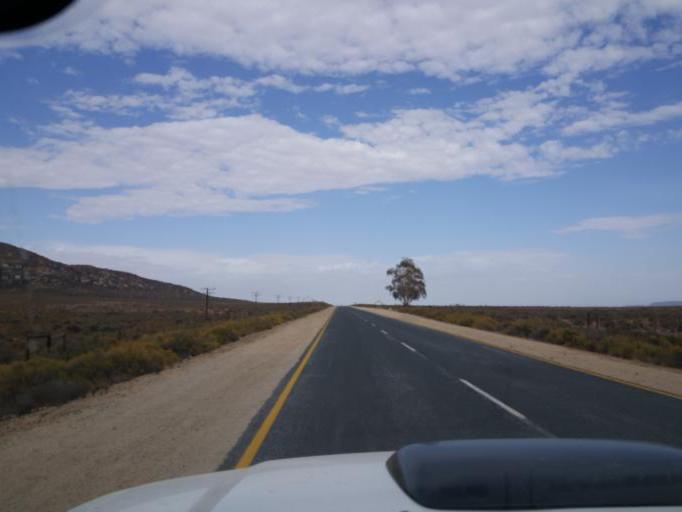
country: ZA
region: Northern Cape
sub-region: Namakwa District Municipality
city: Springbok
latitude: -29.2288
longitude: 17.6818
